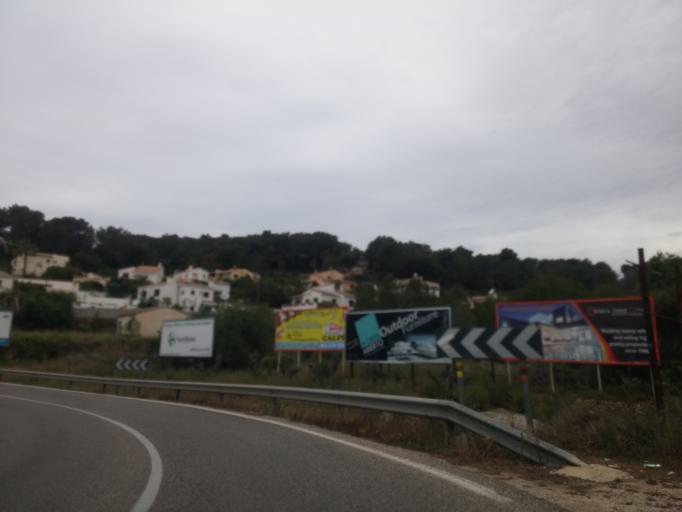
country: ES
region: Valencia
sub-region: Provincia de Alicante
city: Moraira
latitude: 38.6739
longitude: 0.0883
